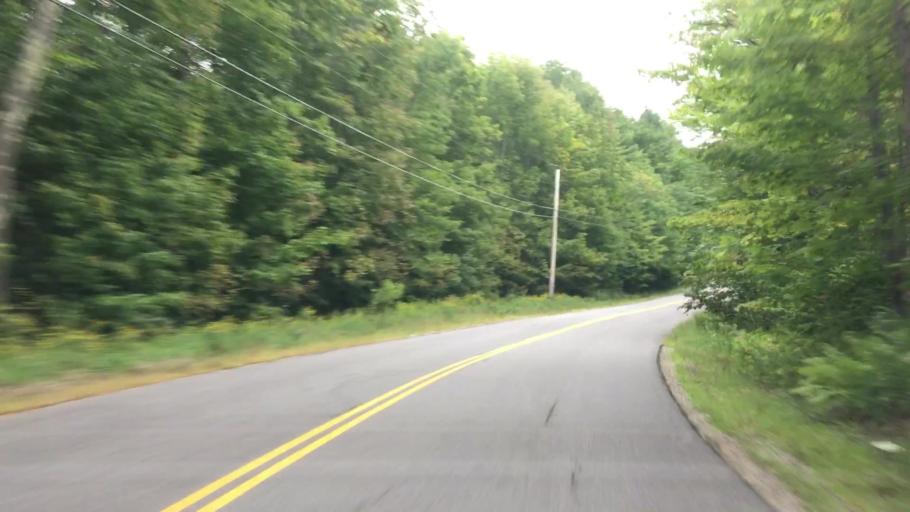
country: US
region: Maine
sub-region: Cumberland County
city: New Gloucester
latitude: 43.9066
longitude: -70.2191
